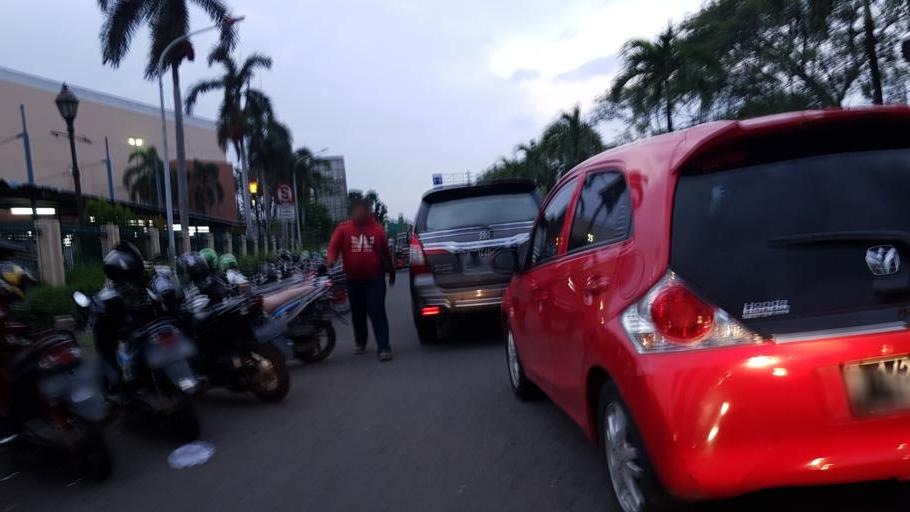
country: ID
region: West Java
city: Ciputat
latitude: -6.1867
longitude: 106.7337
